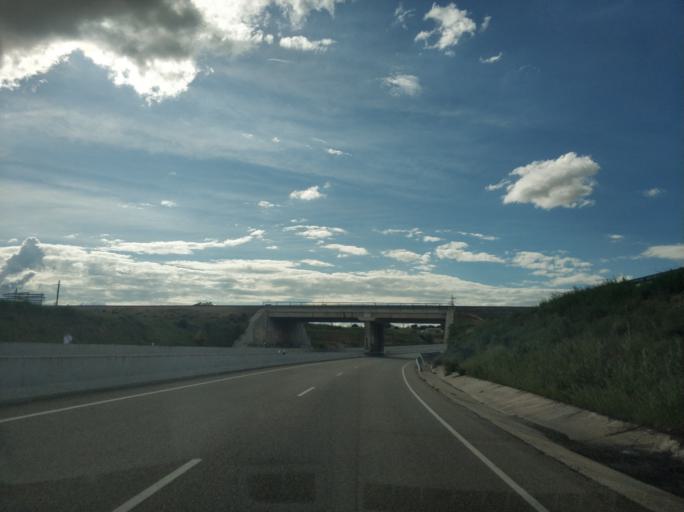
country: ES
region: Castille and Leon
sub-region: Provincia de Burgos
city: Aranda de Duero
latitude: 41.6931
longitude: -3.6720
